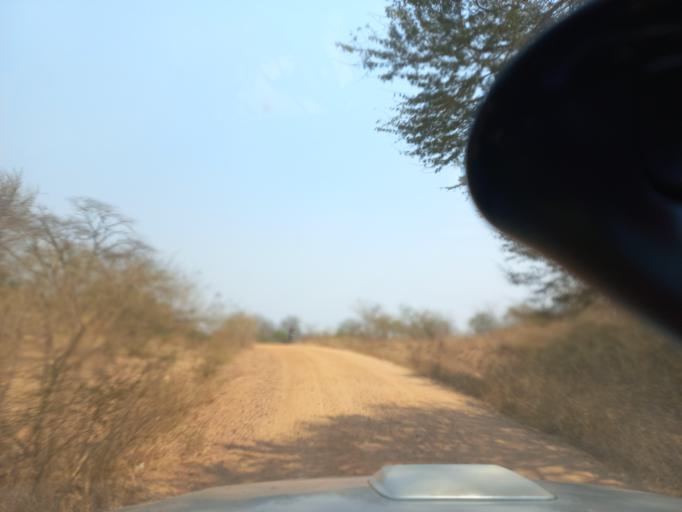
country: ZW
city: Chirundu
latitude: -15.9411
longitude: 28.8220
